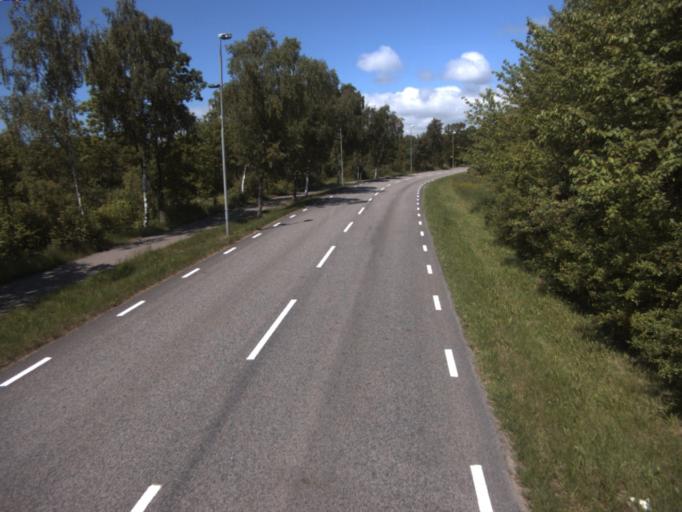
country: SE
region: Skane
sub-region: Helsingborg
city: Helsingborg
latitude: 56.0734
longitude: 12.6925
